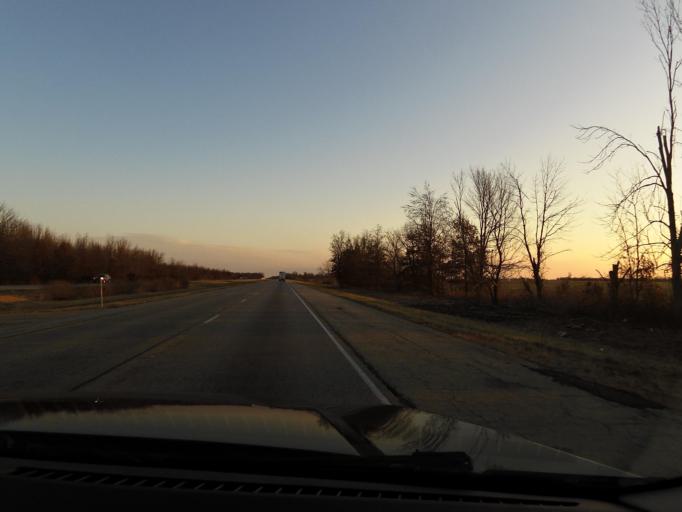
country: US
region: Illinois
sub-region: Marion County
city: Salem
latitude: 38.6995
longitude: -88.9567
